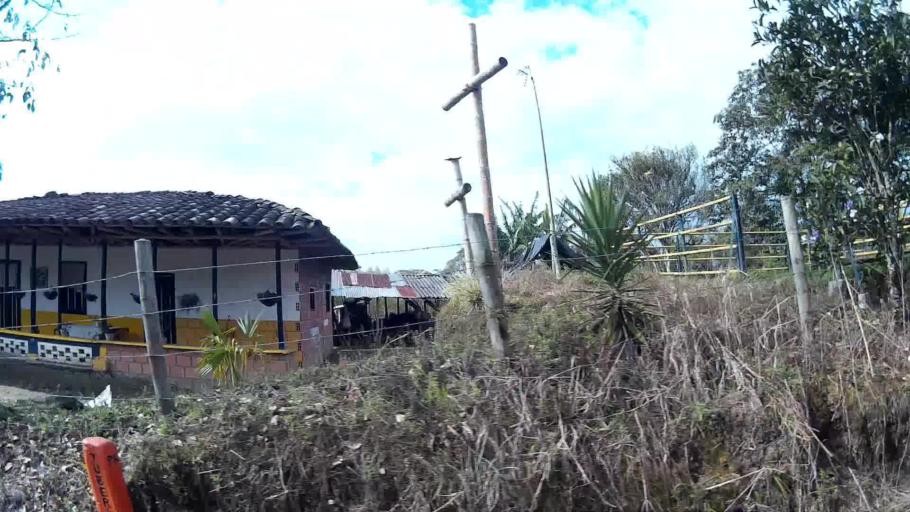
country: CO
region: Quindio
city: Filandia
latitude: 4.6893
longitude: -75.6706
